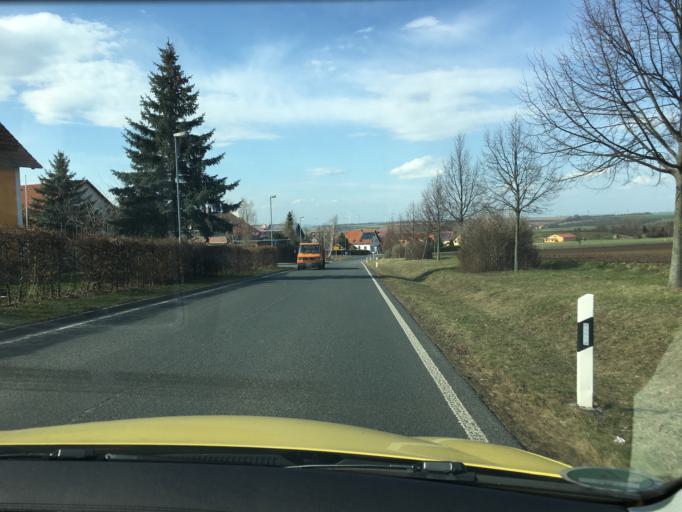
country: DE
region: Thuringia
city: Ballstedt
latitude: 51.0534
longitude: 11.2141
